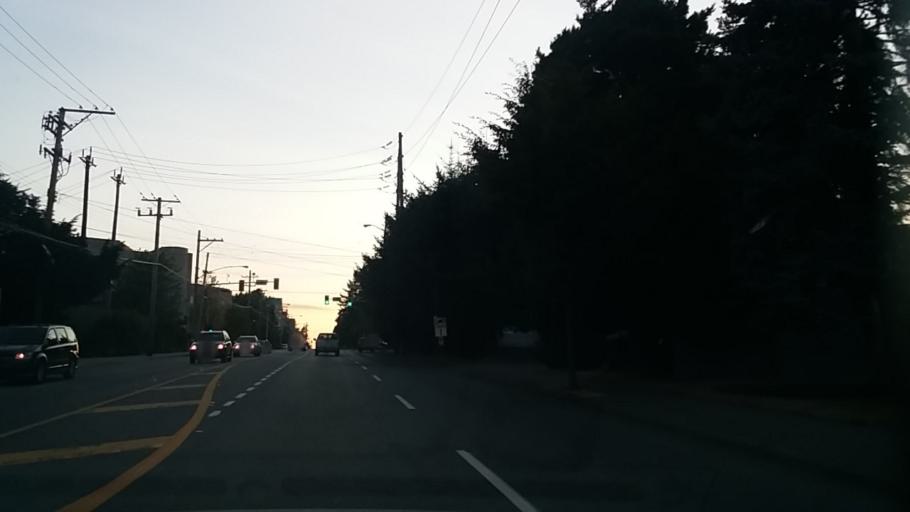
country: CA
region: British Columbia
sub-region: Greater Vancouver Regional District
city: White Rock
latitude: 49.0312
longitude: -122.7893
